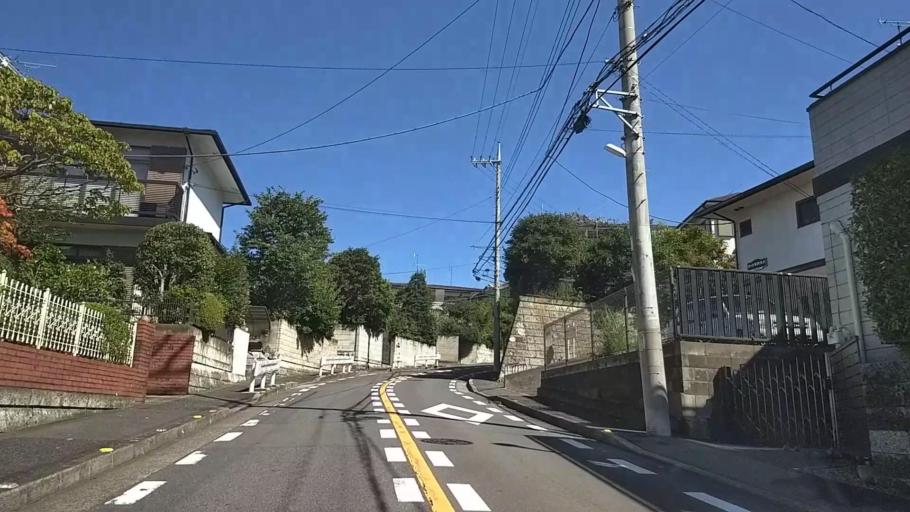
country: JP
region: Tokyo
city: Chofugaoka
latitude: 35.5983
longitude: 139.5217
